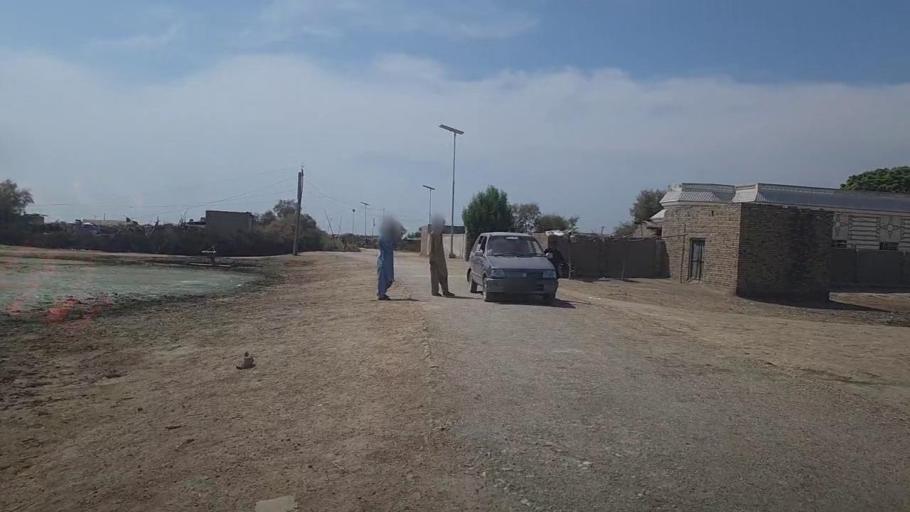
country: PK
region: Sindh
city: Kandhkot
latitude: 28.3109
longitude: 69.2271
